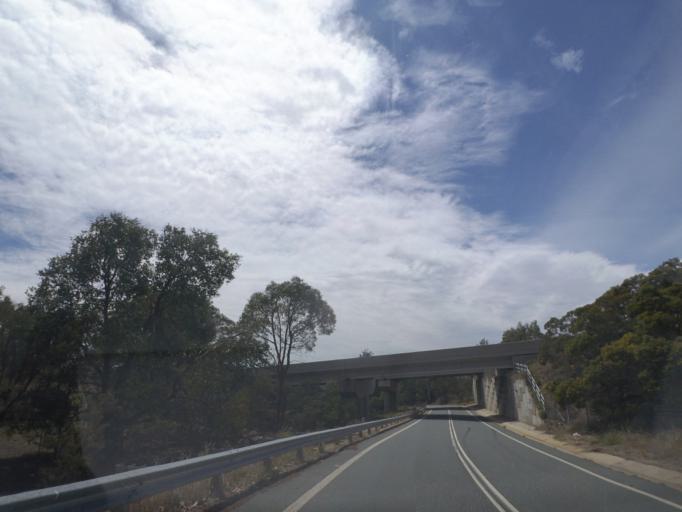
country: AU
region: New South Wales
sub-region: Yass Valley
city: Gundaroo
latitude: -35.1002
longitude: 149.3739
